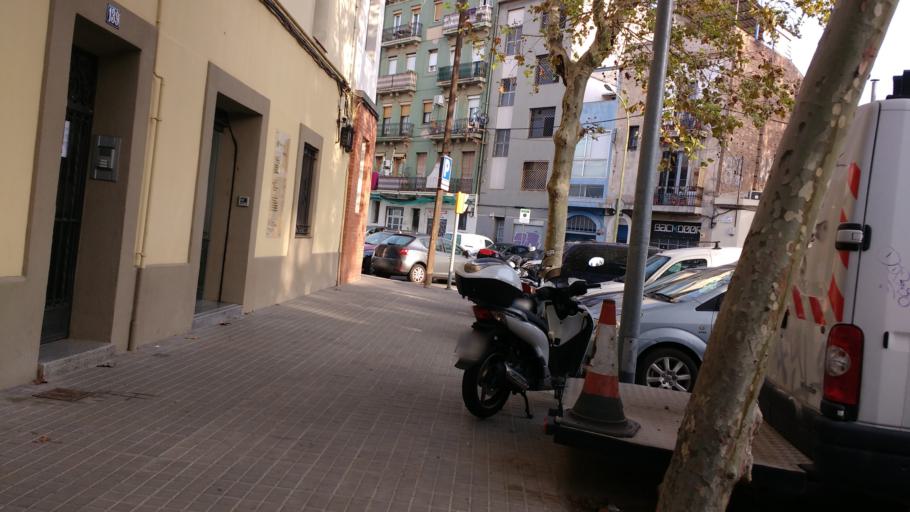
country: ES
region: Catalonia
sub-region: Provincia de Barcelona
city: Sant Marti
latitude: 41.3955
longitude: 2.1991
